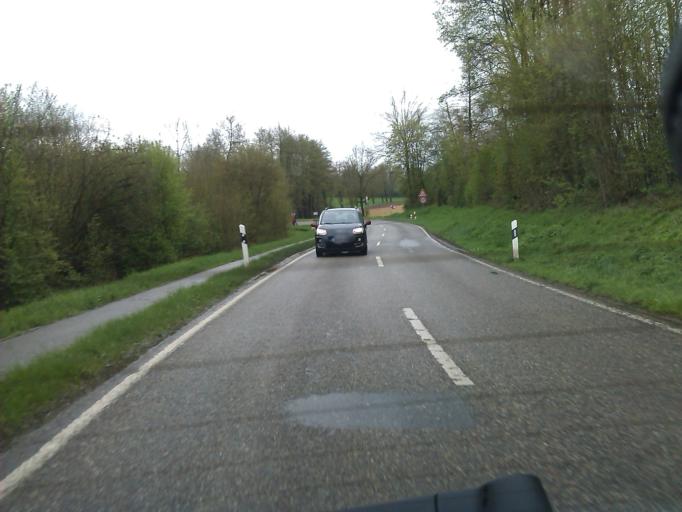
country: DE
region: Baden-Wuerttemberg
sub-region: Regierungsbezirk Stuttgart
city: Bad Wimpfen
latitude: 49.2374
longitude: 9.1455
